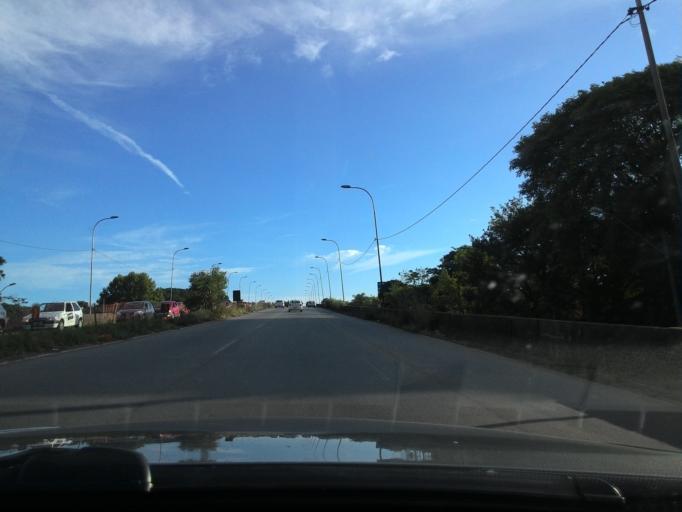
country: BR
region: Parana
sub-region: Pinhais
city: Pinhais
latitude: -25.4254
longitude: -49.2272
